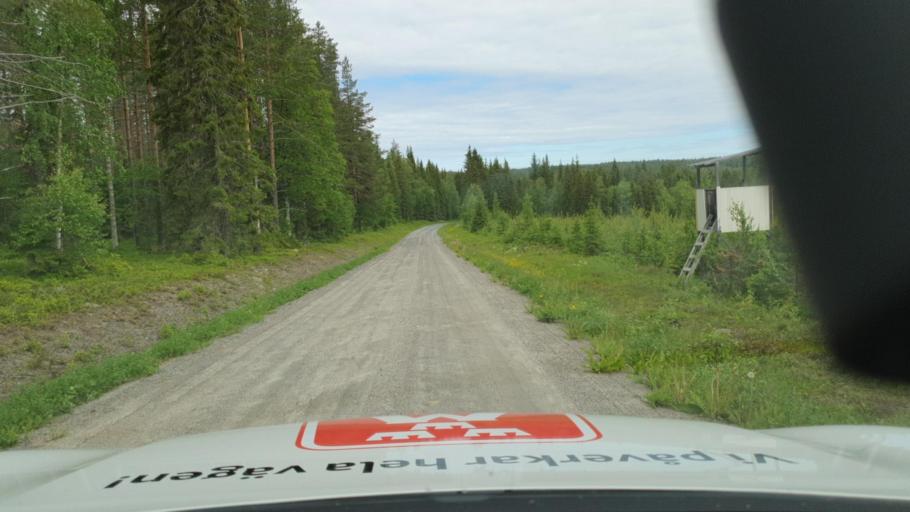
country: SE
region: Vaesterbotten
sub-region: Skelleftea Kommun
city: Langsele
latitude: 64.4660
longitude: 20.2722
